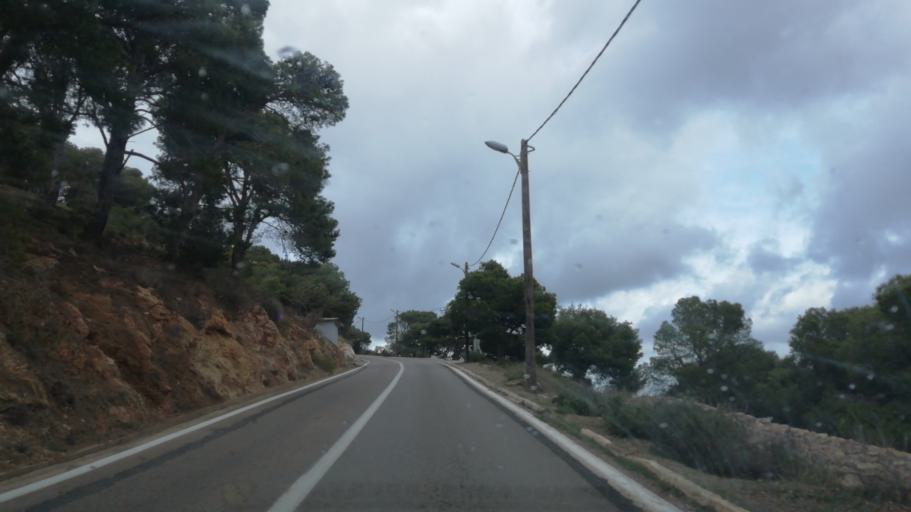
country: DZ
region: Oran
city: Oran
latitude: 35.7079
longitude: -0.6619
